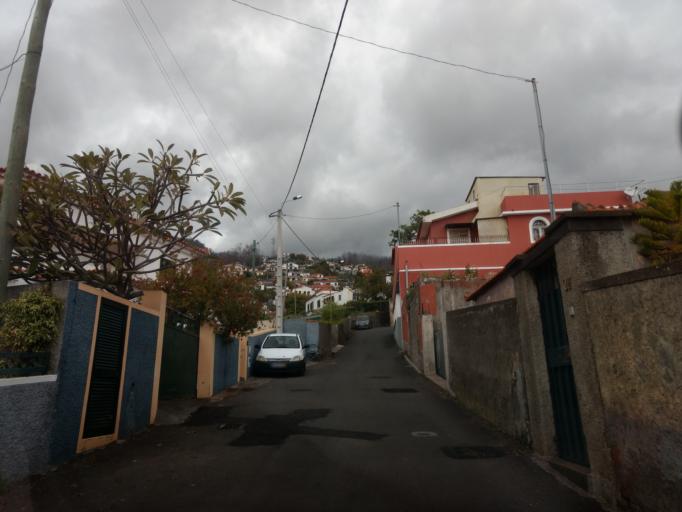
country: PT
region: Madeira
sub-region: Funchal
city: Nossa Senhora do Monte
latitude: 32.6701
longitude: -16.9348
